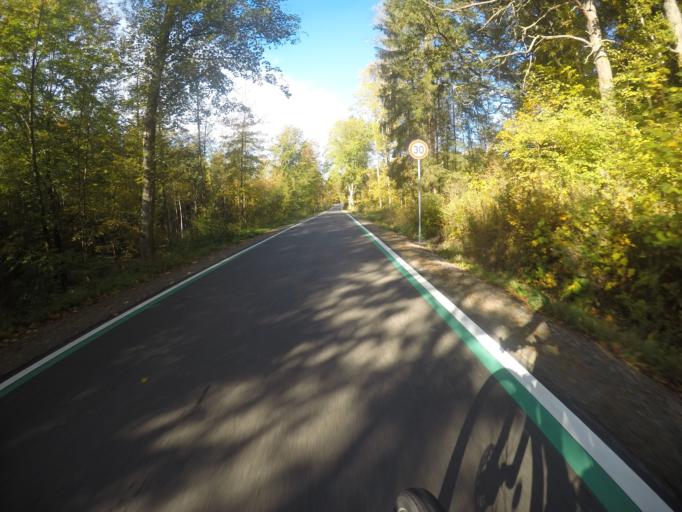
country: DE
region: Baden-Wuerttemberg
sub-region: Regierungsbezirk Stuttgart
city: Sindelfingen
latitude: 48.7028
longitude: 9.0548
